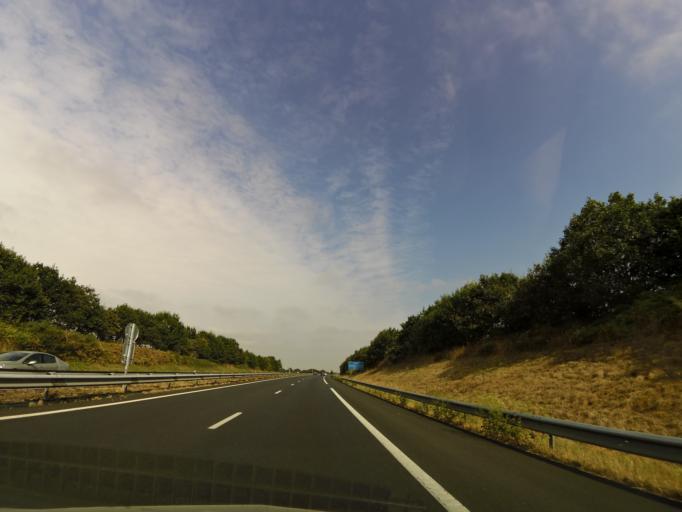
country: FR
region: Pays de la Loire
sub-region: Departement de la Vendee
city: Chauche
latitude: 46.8514
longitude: -1.2743
